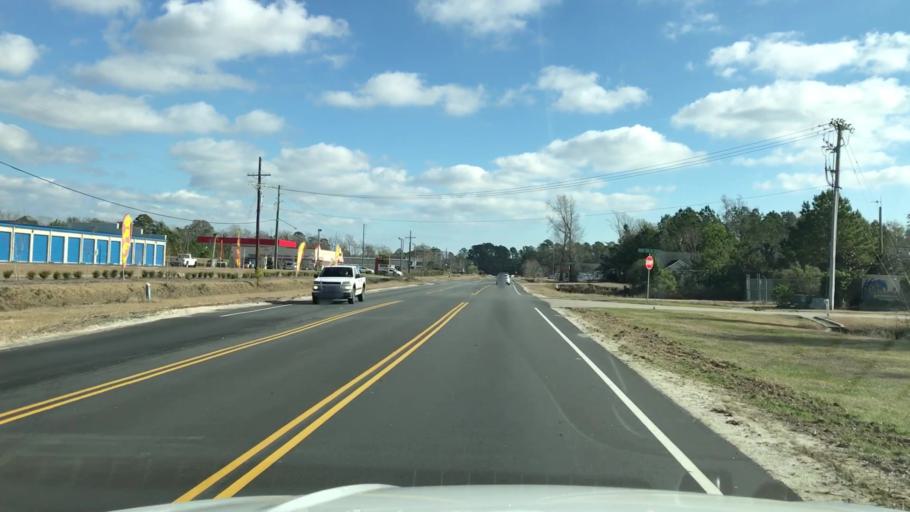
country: US
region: South Carolina
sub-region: Horry County
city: Socastee
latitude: 33.6770
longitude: -78.9772
